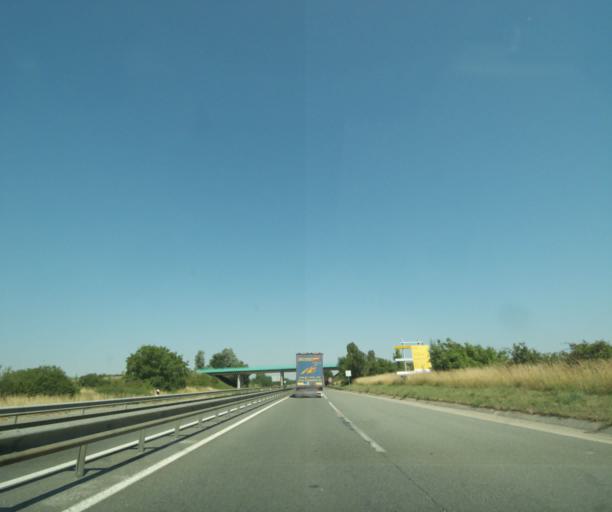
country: FR
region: Champagne-Ardenne
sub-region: Departement de la Haute-Marne
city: Saint-Dizier
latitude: 48.6263
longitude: 4.9341
